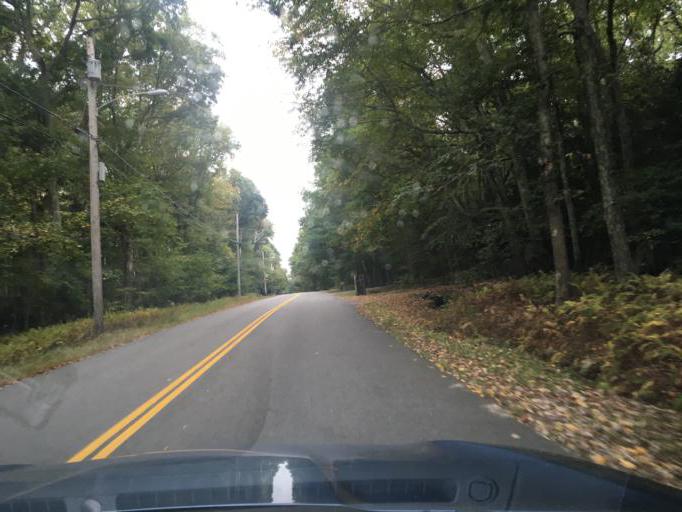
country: US
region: Rhode Island
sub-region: Washington County
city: Exeter
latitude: 41.6166
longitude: -71.5369
